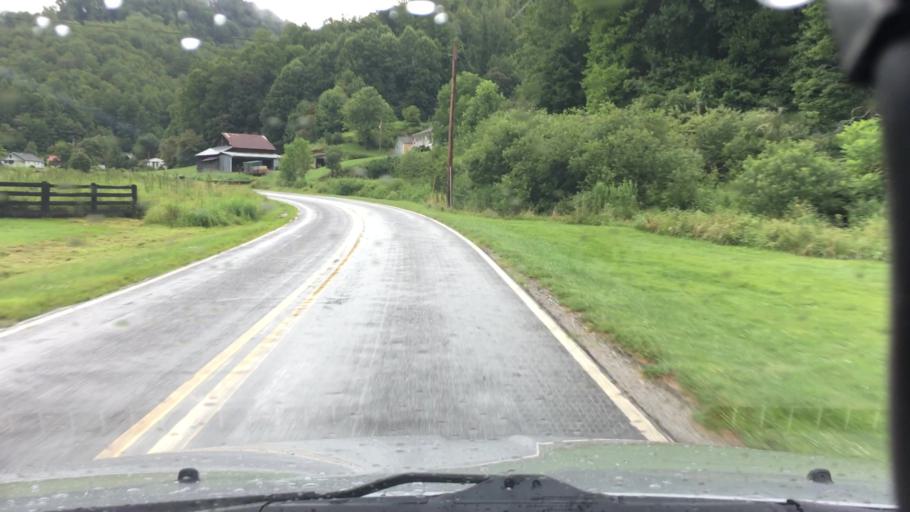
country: US
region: North Carolina
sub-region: Madison County
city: Mars Hill
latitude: 35.9117
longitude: -82.4751
